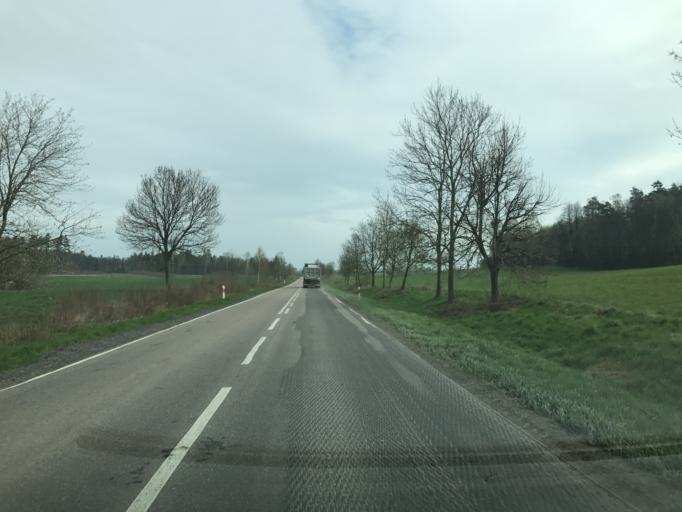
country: PL
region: Warmian-Masurian Voivodeship
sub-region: Powiat ostrodzki
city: Gierzwald
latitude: 53.5526
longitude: 20.0908
